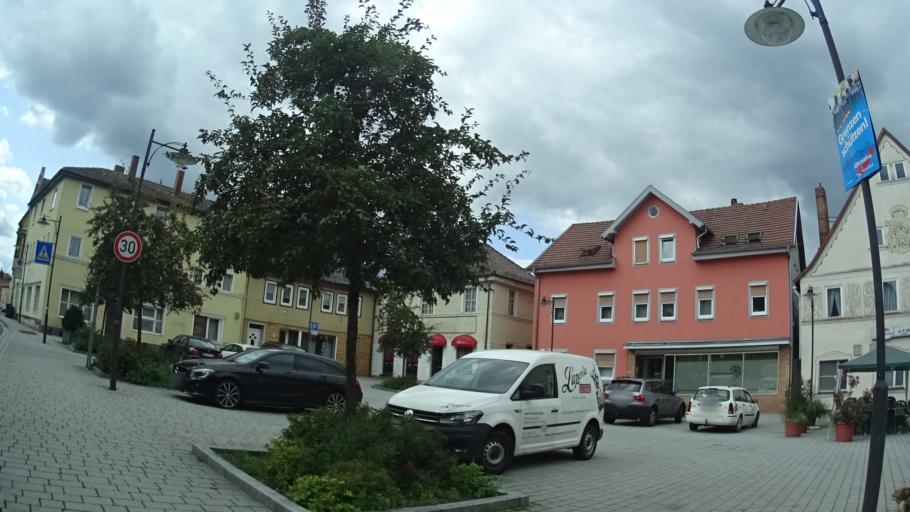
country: DE
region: Bavaria
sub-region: Upper Franconia
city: Neustadt bei Coburg
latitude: 50.3270
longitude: 11.1222
